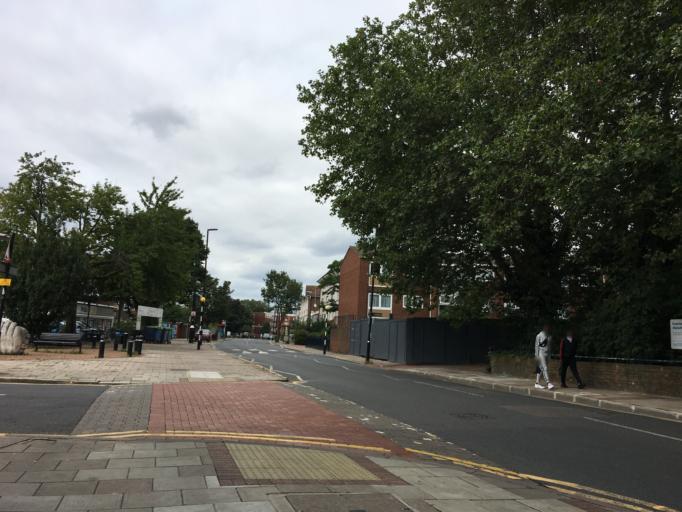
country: GB
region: England
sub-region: Greater London
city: East Ham
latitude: 51.5112
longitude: 0.0256
